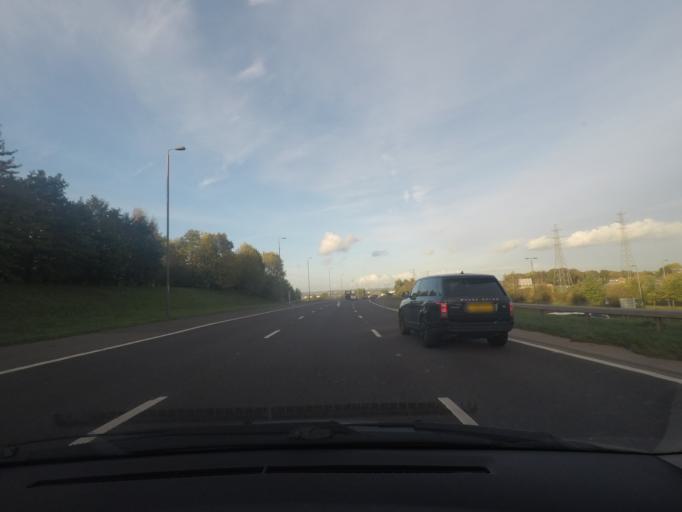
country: GB
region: England
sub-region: City and Borough of Leeds
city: Lofthouse
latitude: 53.7552
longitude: -1.5150
